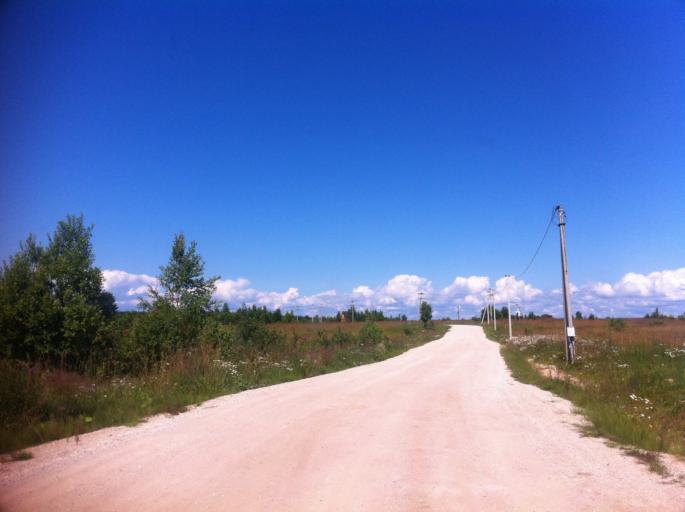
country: RU
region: Pskov
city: Izborsk
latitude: 57.8245
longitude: 27.9654
